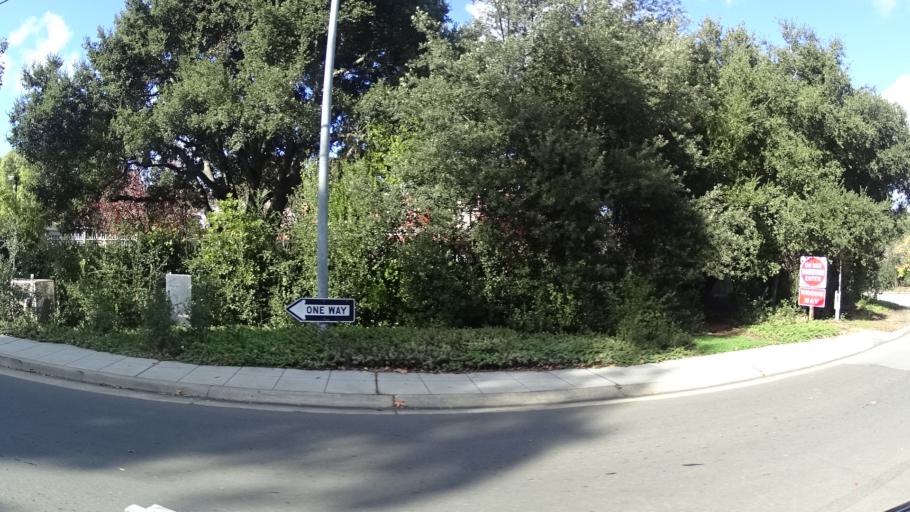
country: US
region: California
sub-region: Santa Clara County
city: Mountain View
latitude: 37.3850
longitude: -122.0630
